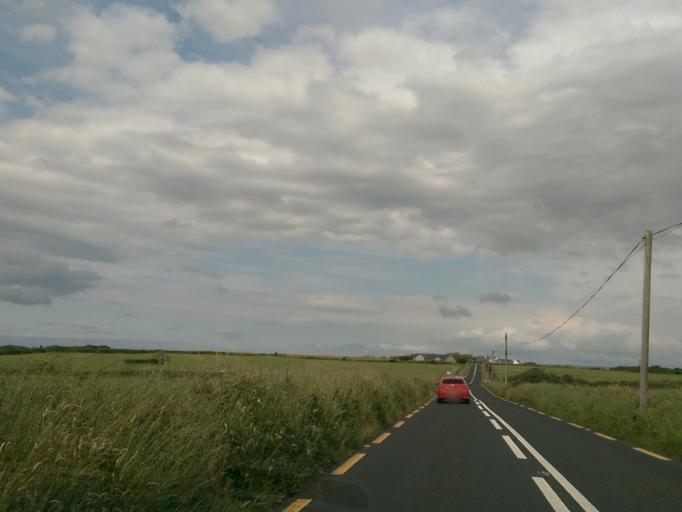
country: IE
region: Munster
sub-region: An Clar
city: Kilrush
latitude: 52.7639
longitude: -9.4542
